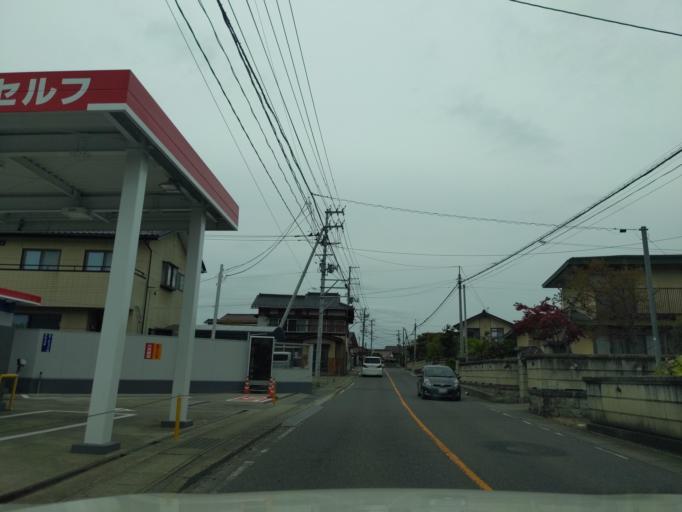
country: JP
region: Fukushima
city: Koriyama
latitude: 37.3479
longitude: 140.3690
